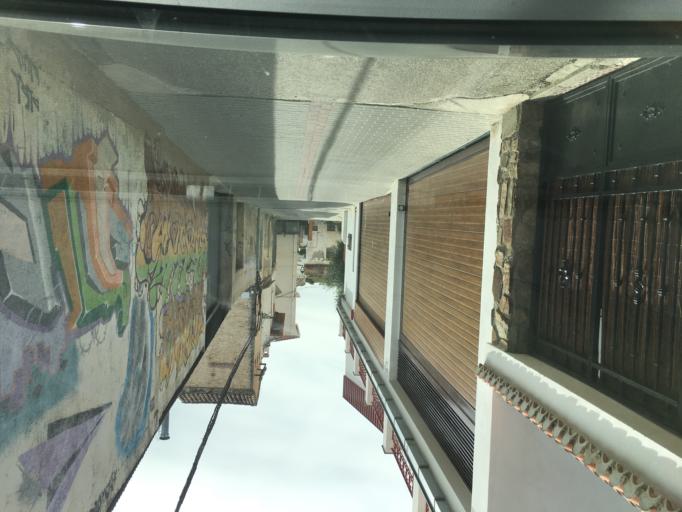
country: ES
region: Andalusia
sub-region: Provincia de Granada
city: Beas de Granada
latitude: 37.2167
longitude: -3.4817
